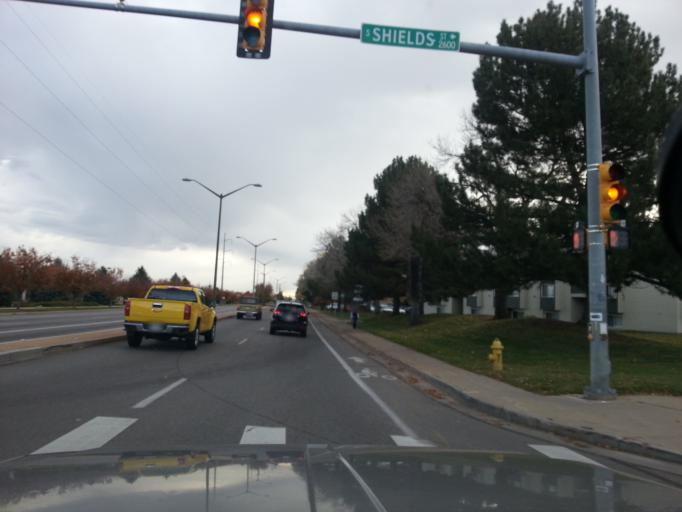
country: US
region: Colorado
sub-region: Larimer County
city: Fort Collins
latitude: 40.5526
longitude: -105.0961
